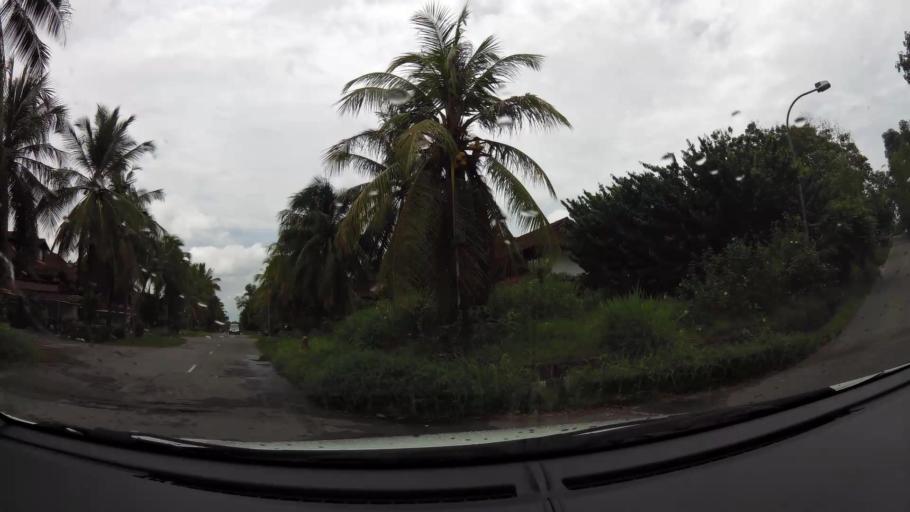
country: BN
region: Brunei and Muara
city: Bandar Seri Begawan
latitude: 4.8932
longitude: 114.9211
